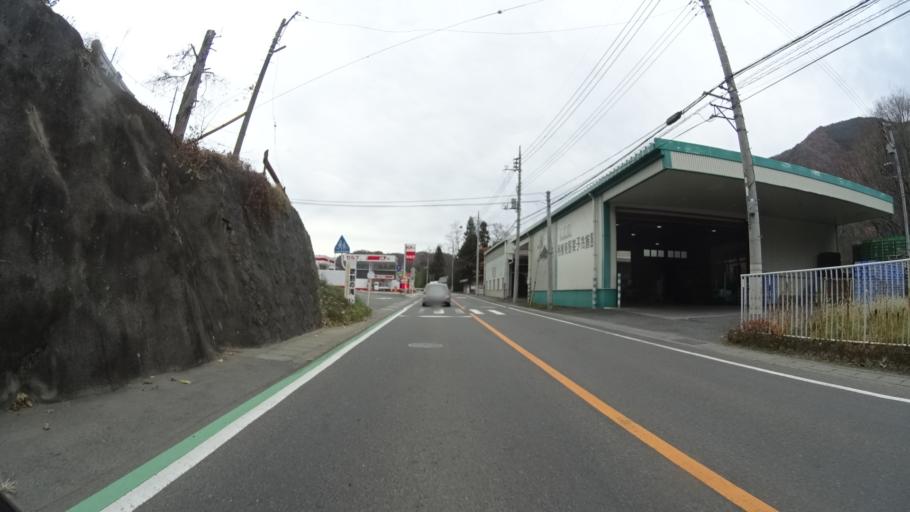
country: JP
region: Gunma
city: Numata
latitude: 36.6913
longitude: 139.2081
